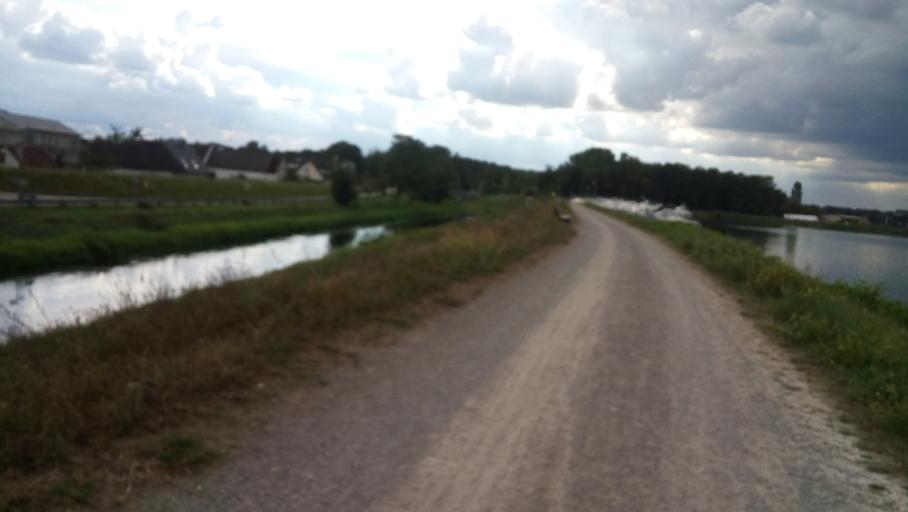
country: DE
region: Baden-Wuerttemberg
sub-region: Karlsruhe Region
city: Greffern
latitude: 48.7573
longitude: 8.0057
